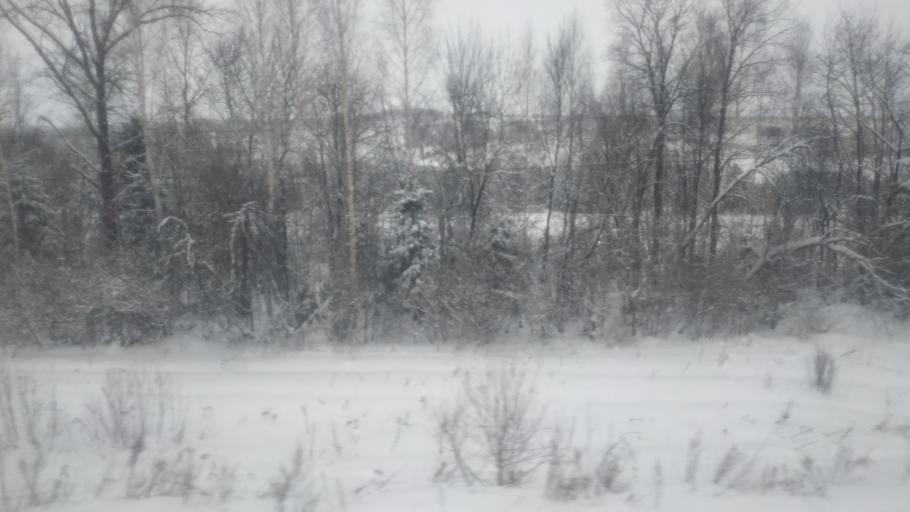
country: RU
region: Udmurtiya
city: Kiyasovo
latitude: 56.5016
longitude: 53.3755
